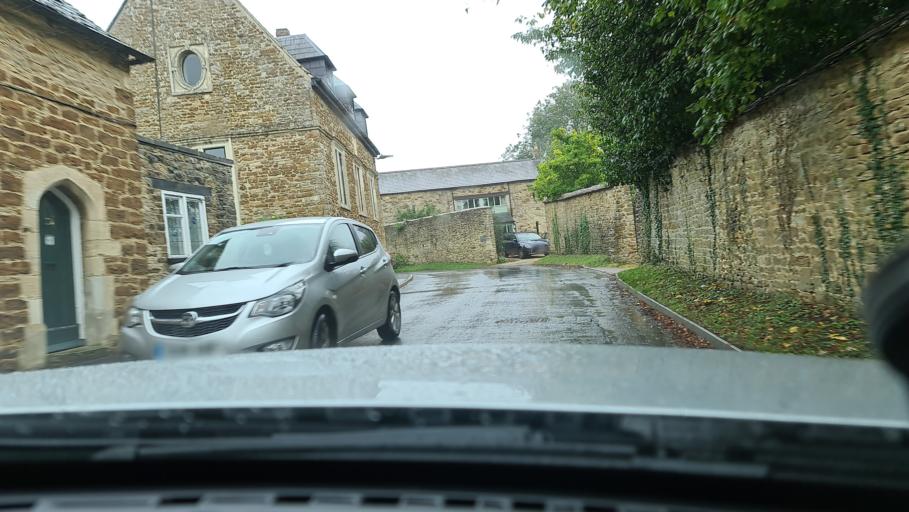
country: GB
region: England
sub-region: Oxfordshire
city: Somerton
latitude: 51.9305
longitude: -1.3107
